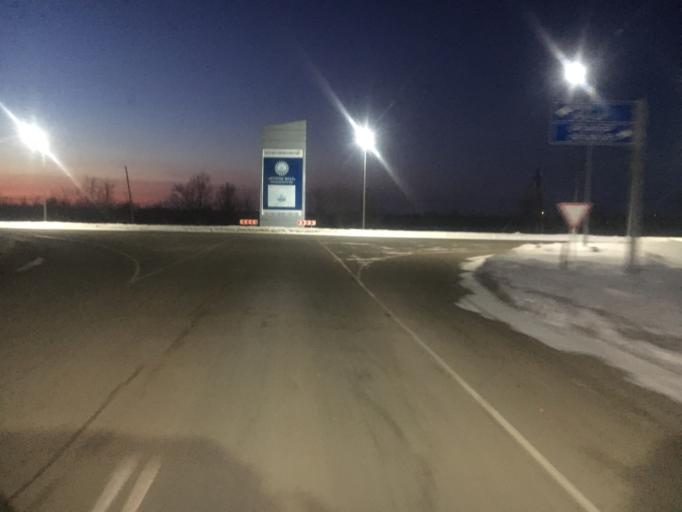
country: KZ
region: Batys Qazaqstan
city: Oral
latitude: 51.1652
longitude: 51.5241
